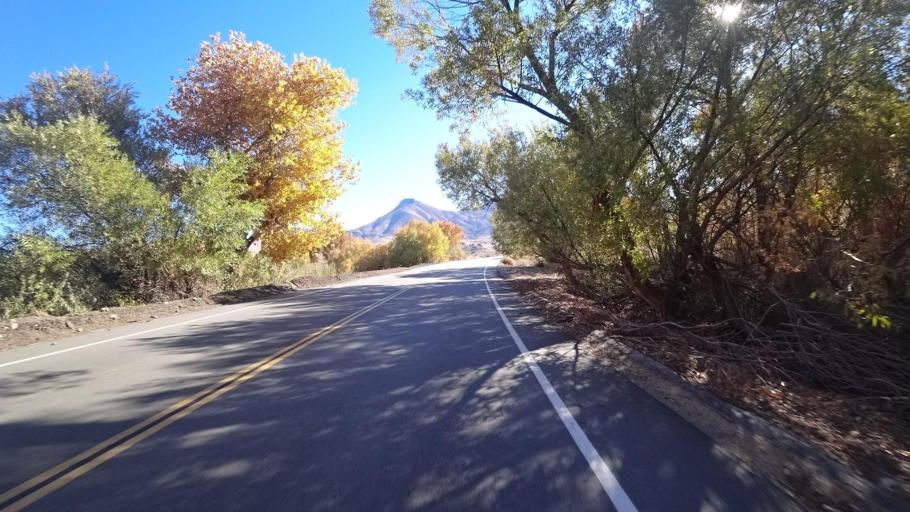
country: US
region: California
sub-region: Kern County
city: Weldon
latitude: 35.6688
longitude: -118.3230
